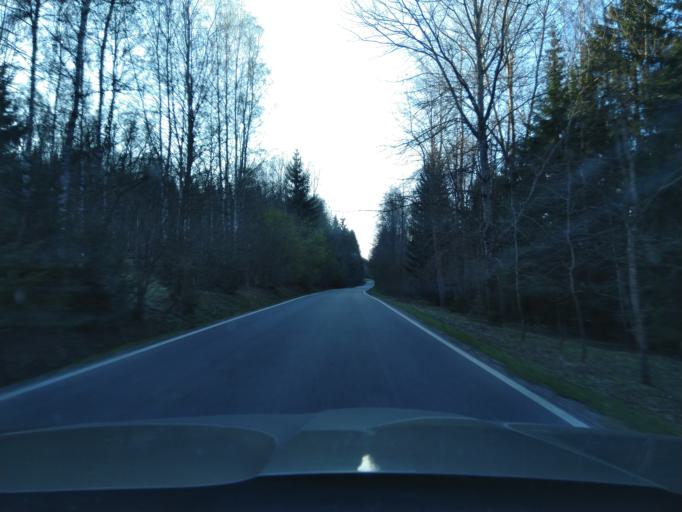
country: CZ
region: Jihocesky
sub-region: Okres Prachatice
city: Vimperk
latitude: 48.9524
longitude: 13.7794
